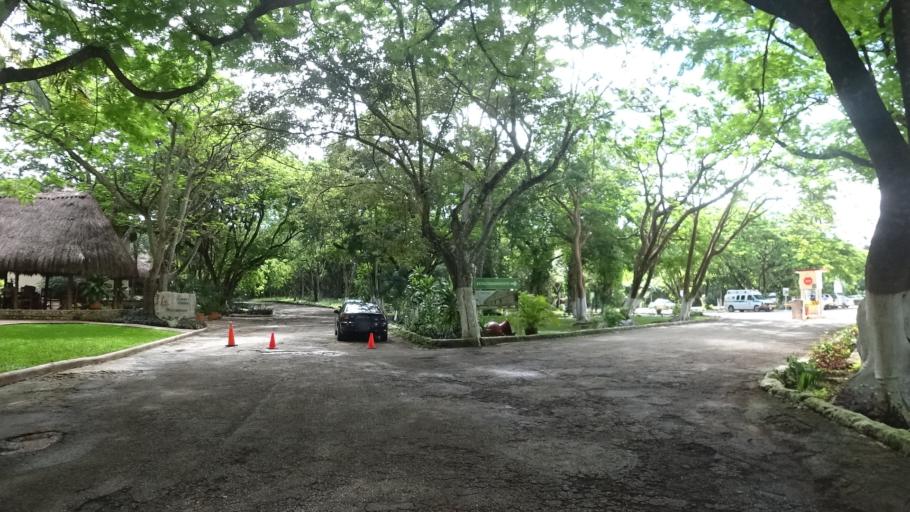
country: MX
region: Yucatan
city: Santa Elena
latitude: 20.3612
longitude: -89.7675
